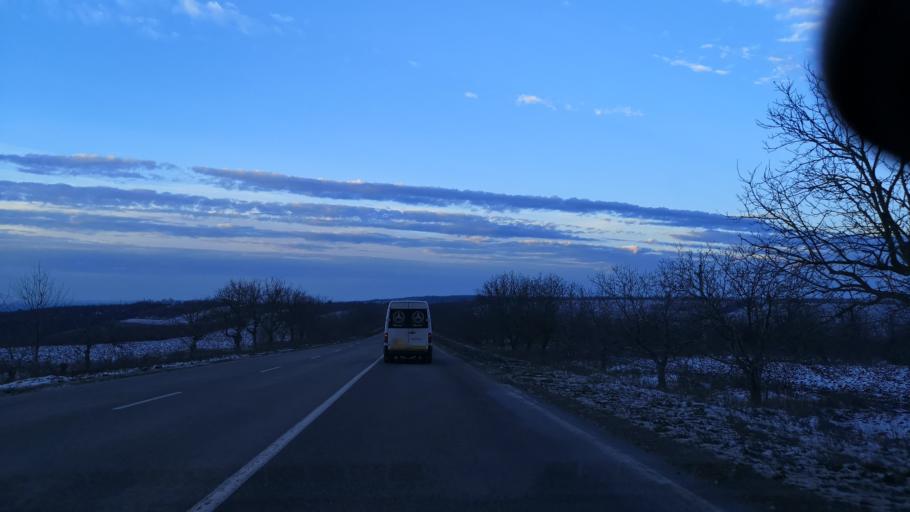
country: MD
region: Orhei
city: Orhei
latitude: 47.5405
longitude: 28.7931
